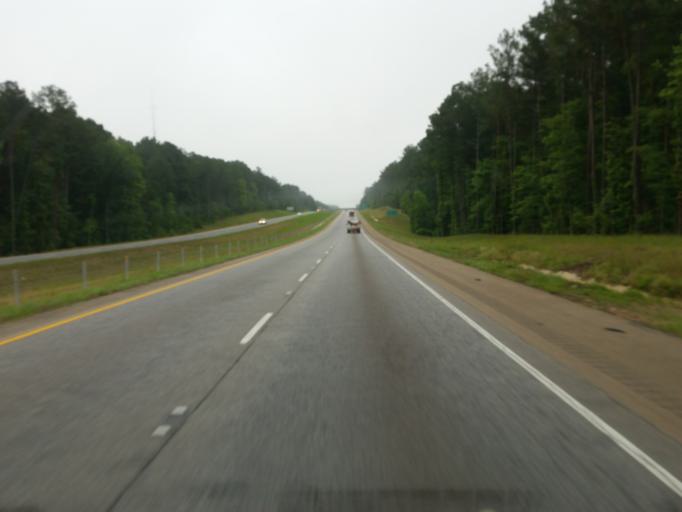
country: US
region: Louisiana
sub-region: Webster Parish
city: Minden
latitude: 32.5782
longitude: -93.2378
